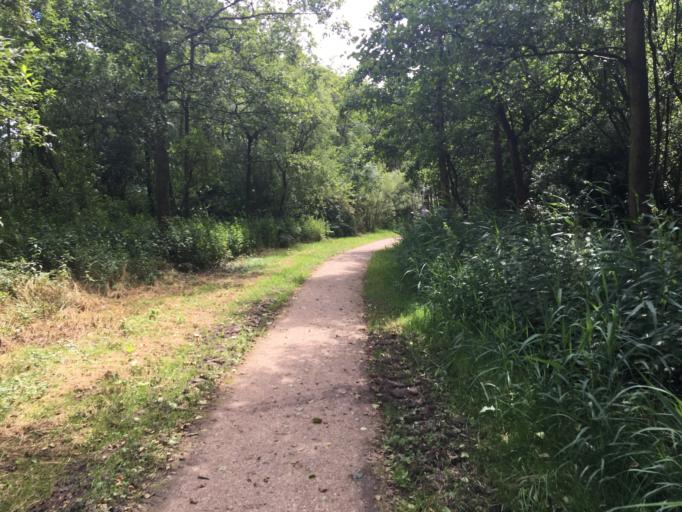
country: NL
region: South Holland
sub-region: Gemeente Gouda
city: Gouda
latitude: 52.0189
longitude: 4.7345
